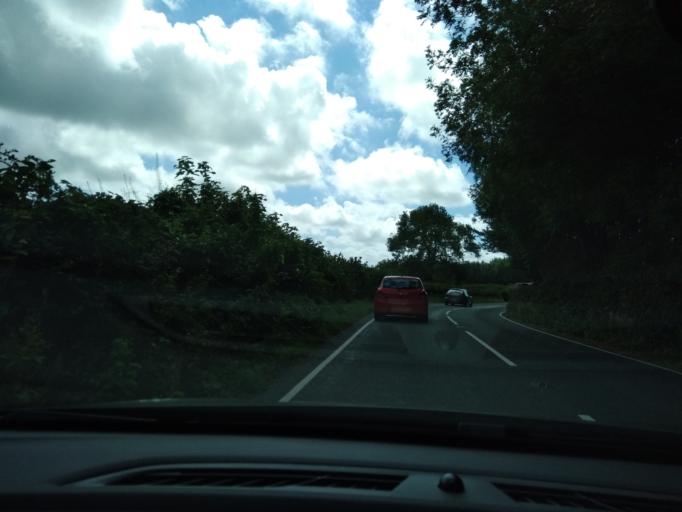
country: GB
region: England
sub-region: Cumbria
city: Millom
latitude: 54.2490
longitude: -3.3060
